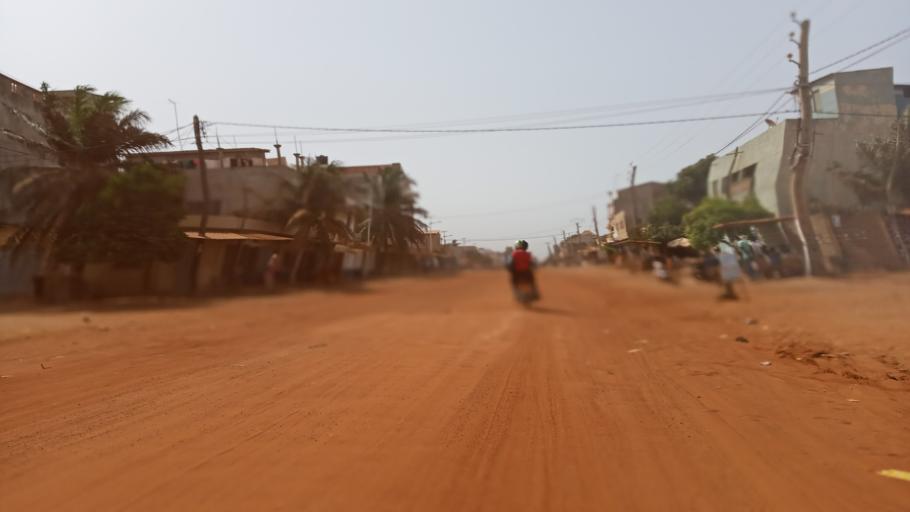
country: TG
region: Maritime
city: Lome
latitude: 6.1973
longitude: 1.1730
